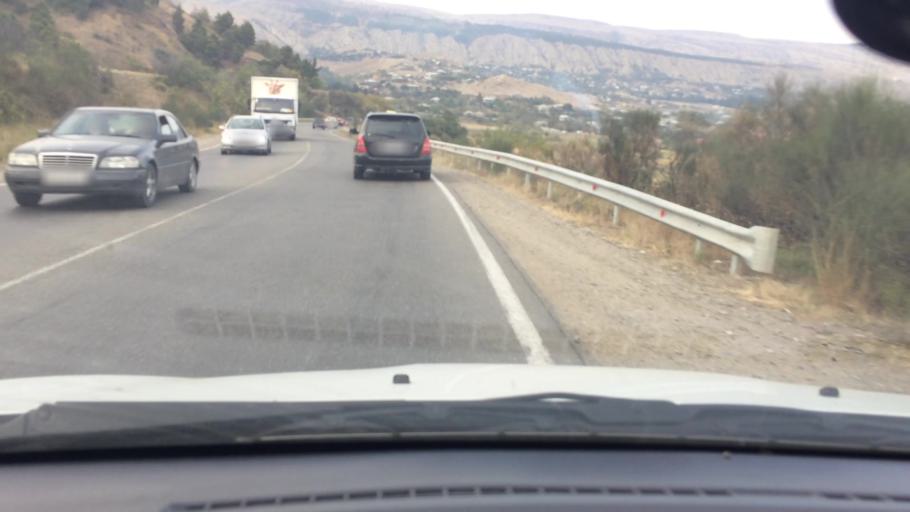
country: GE
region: T'bilisi
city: Tbilisi
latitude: 41.5941
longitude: 44.7805
